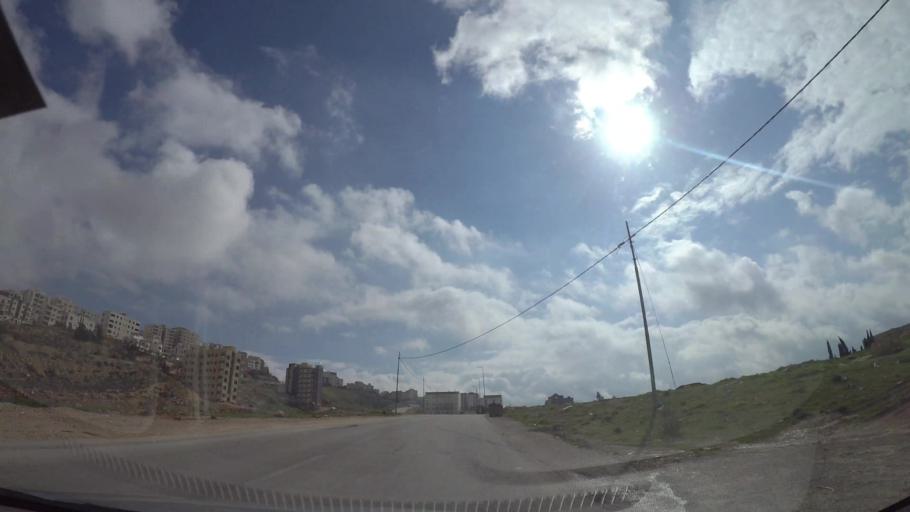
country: JO
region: Amman
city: Al Jubayhah
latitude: 32.0672
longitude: 35.8693
